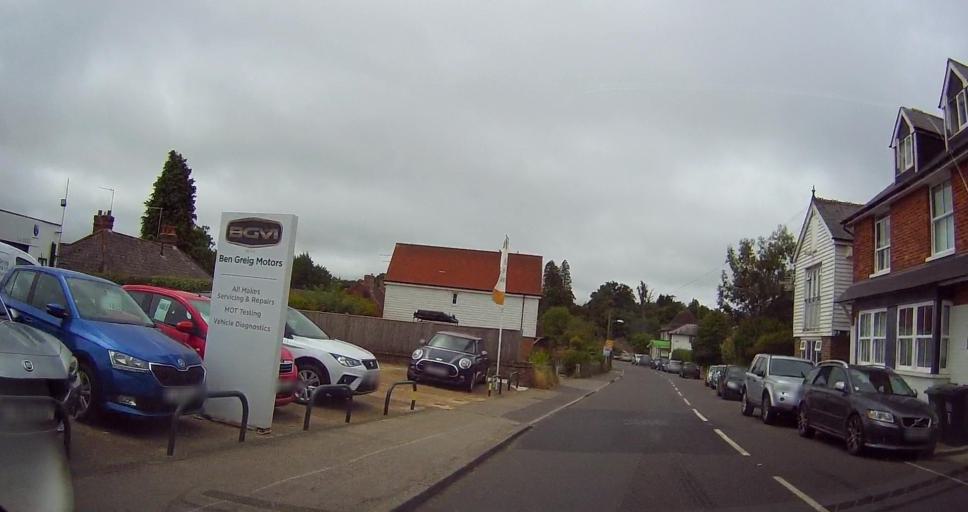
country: GB
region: England
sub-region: East Sussex
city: Wadhurst
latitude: 51.0673
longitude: 0.3338
